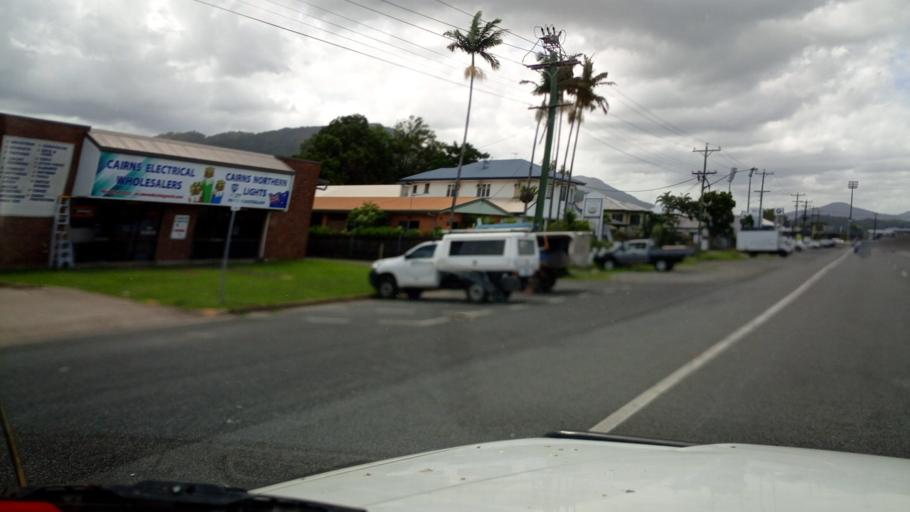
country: AU
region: Queensland
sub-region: Cairns
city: Woree
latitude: -16.9391
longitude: 145.7517
